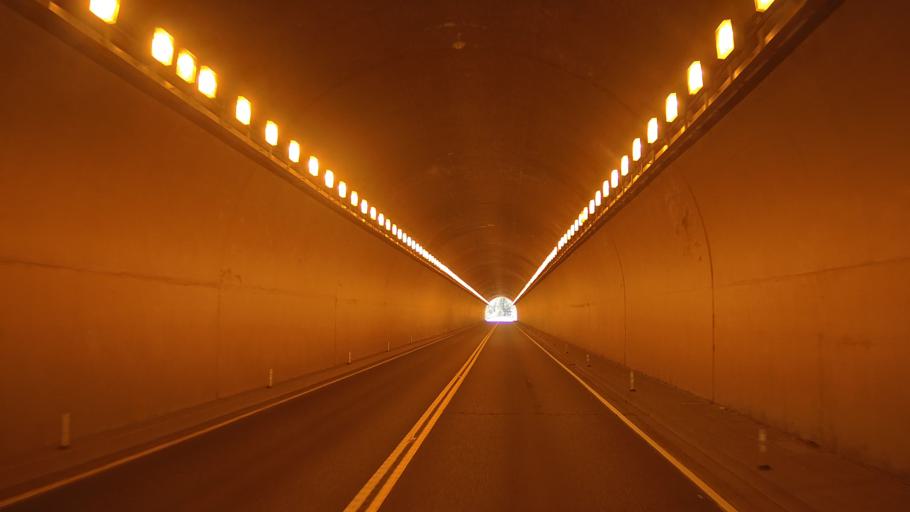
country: CA
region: British Columbia
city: Hope
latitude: 49.5629
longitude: -121.4102
